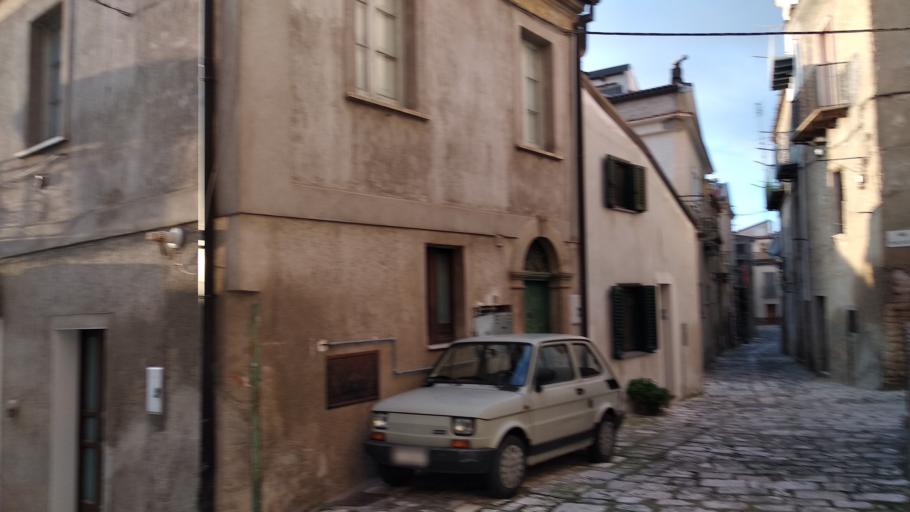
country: IT
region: Basilicate
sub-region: Provincia di Matera
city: Tricarico
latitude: 40.6215
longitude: 16.1462
